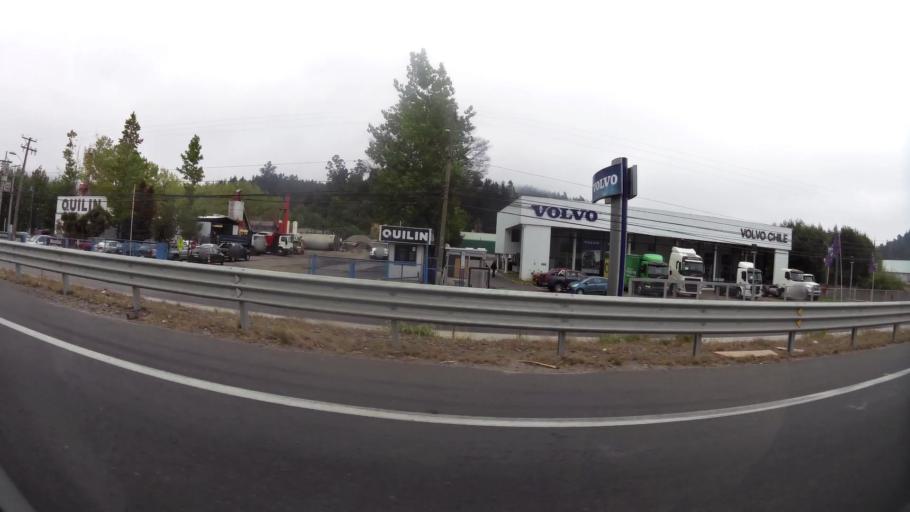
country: CL
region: Biobio
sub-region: Provincia de Concepcion
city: Concepcion
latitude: -36.8189
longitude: -72.9914
